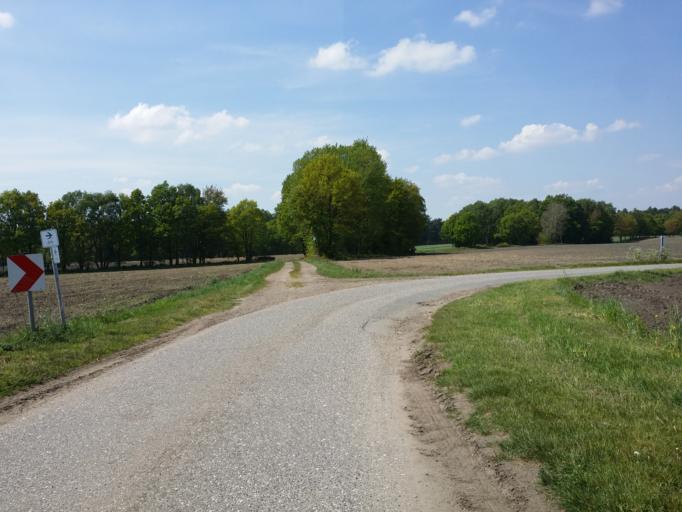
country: DE
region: Lower Saxony
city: Wulsbuttel
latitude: 53.2912
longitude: 8.6599
